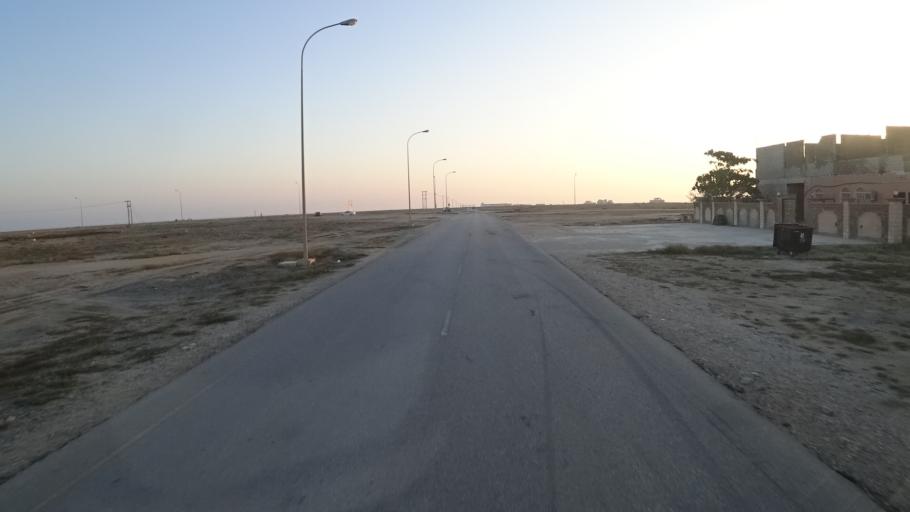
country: OM
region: Zufar
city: Salalah
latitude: 16.9806
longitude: 54.7096
